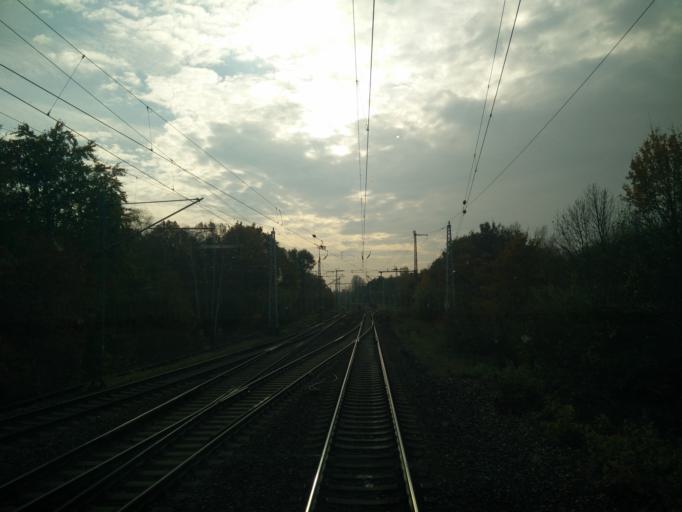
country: DE
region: Berlin
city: Adlershof
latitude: 52.4636
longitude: 13.5515
